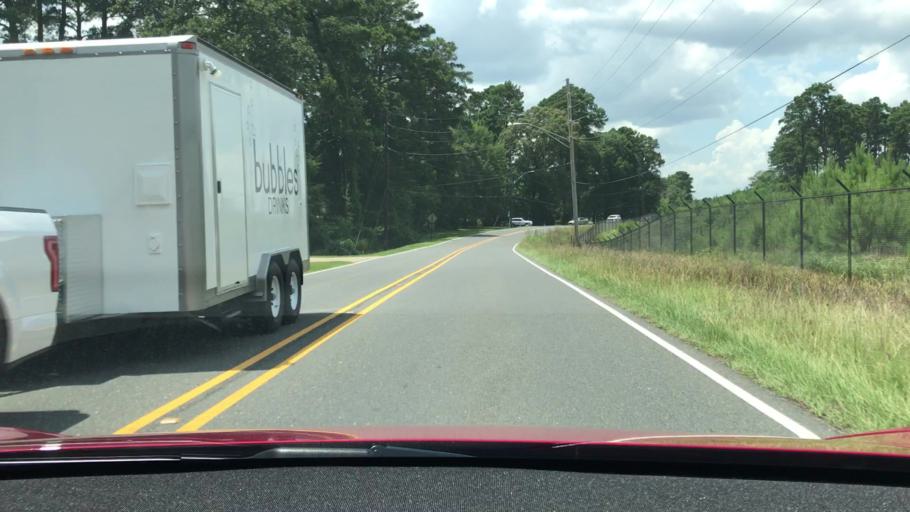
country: US
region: Louisiana
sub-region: Bossier Parish
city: Bossier City
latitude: 32.3848
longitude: -93.7156
